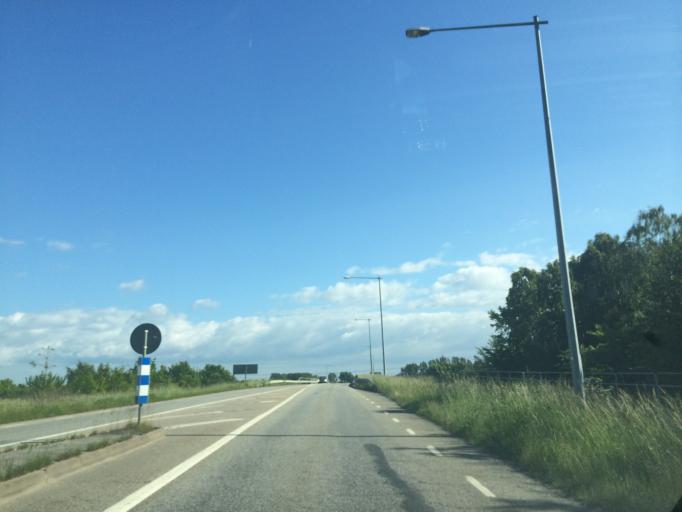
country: SE
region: Skane
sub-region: Kavlinge Kommun
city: Loddekopinge
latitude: 55.7463
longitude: 13.0286
